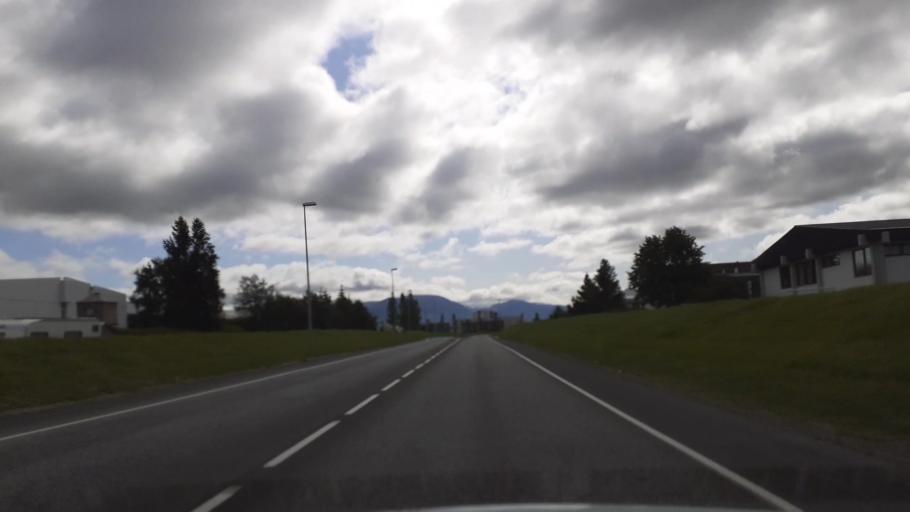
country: IS
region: Northeast
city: Akureyri
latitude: 65.6727
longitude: -18.1086
